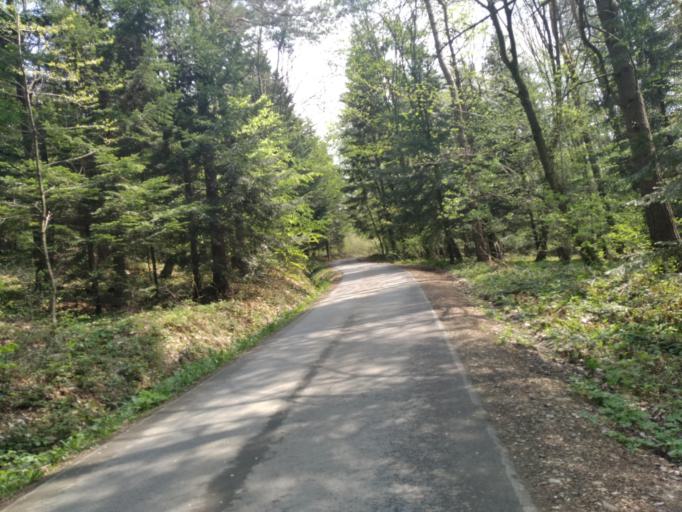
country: PL
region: Subcarpathian Voivodeship
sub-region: Powiat krosnienski
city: Iwonicz-Zdroj
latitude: 49.5427
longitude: 21.7921
